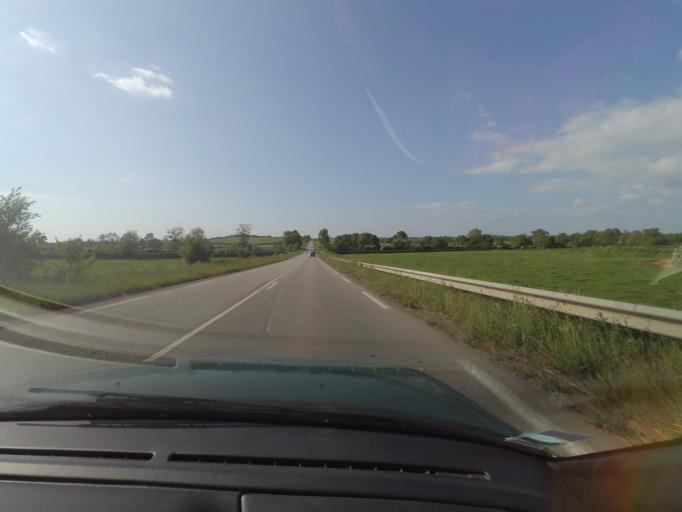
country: FR
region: Pays de la Loire
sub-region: Departement de la Vendee
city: Angles
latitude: 46.4365
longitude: -1.4031
